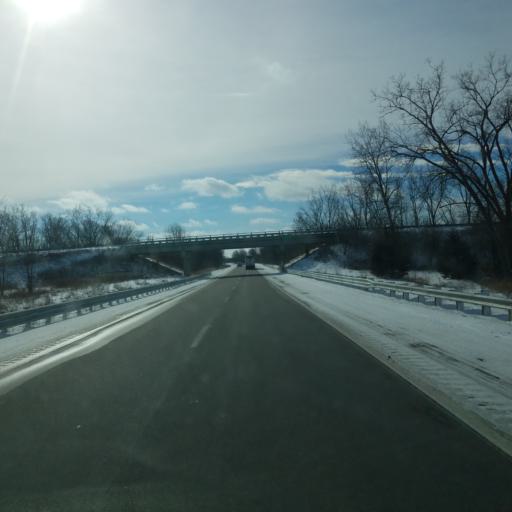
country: US
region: Michigan
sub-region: Gratiot County
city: Ithaca
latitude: 43.3362
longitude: -84.6023
